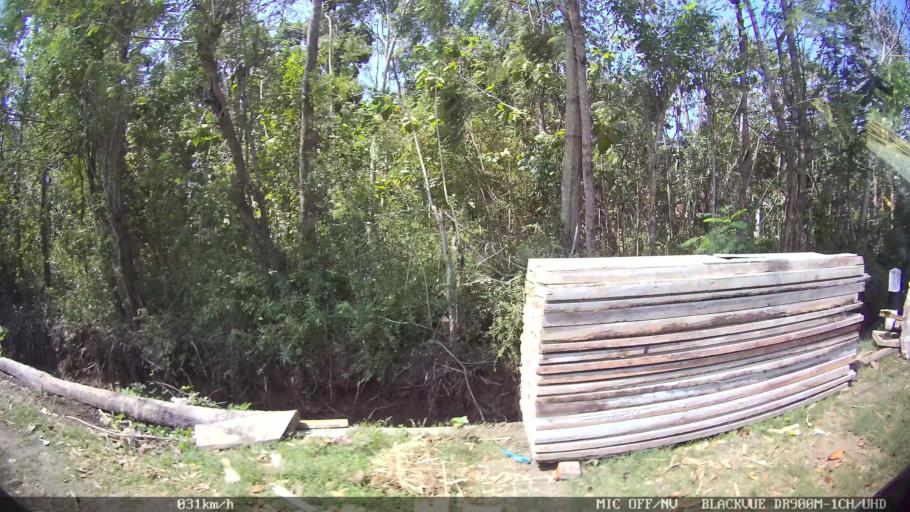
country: ID
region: Daerah Istimewa Yogyakarta
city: Pundong
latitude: -7.9638
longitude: 110.3558
